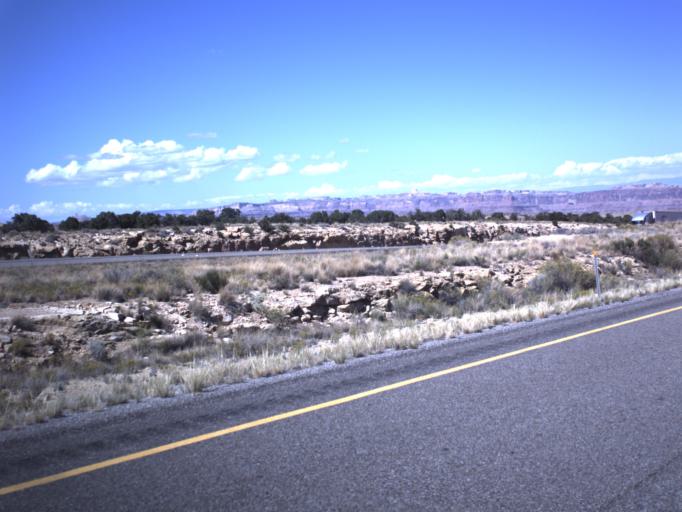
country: US
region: Utah
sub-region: Emery County
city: Castle Dale
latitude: 38.9211
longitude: -110.5002
